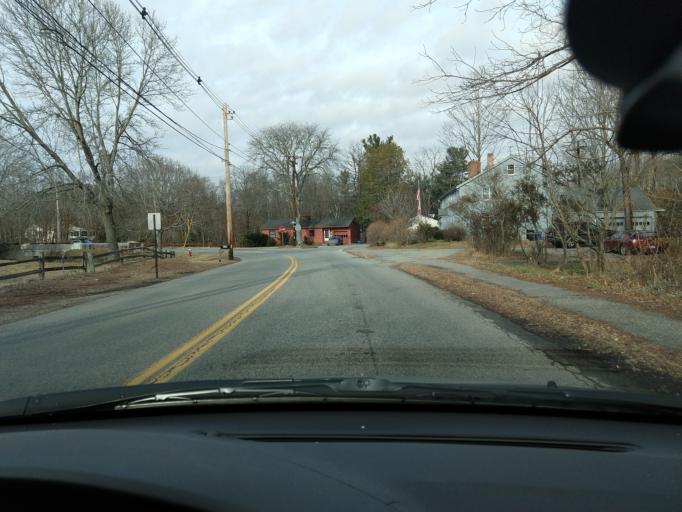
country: US
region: Massachusetts
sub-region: Middlesex County
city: Bedford
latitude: 42.4924
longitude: -71.2559
